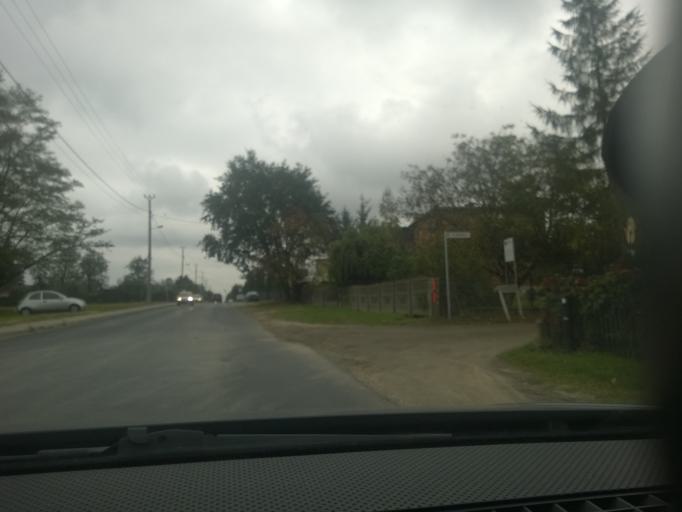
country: PL
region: Greater Poland Voivodeship
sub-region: Powiat kaliski
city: Opatowek
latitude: 51.7245
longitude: 18.1524
